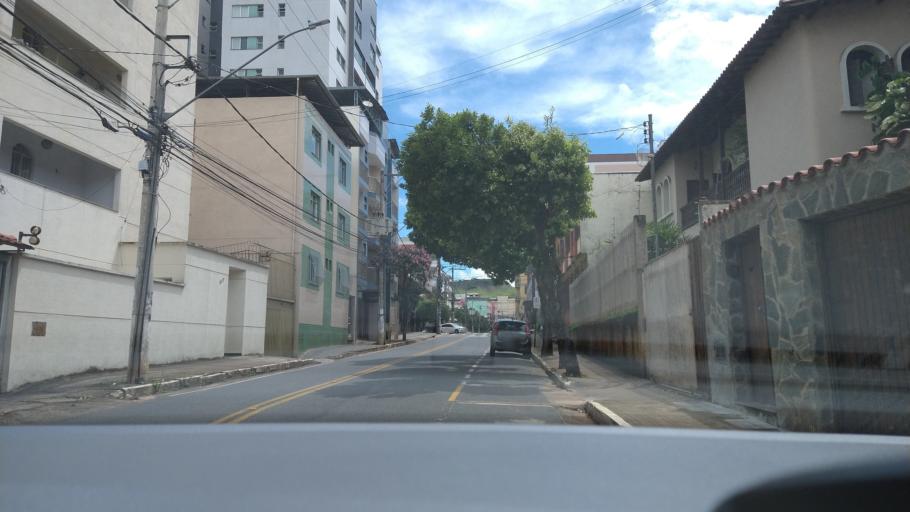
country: BR
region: Minas Gerais
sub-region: Vicosa
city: Vicosa
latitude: -20.7616
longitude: -42.8818
